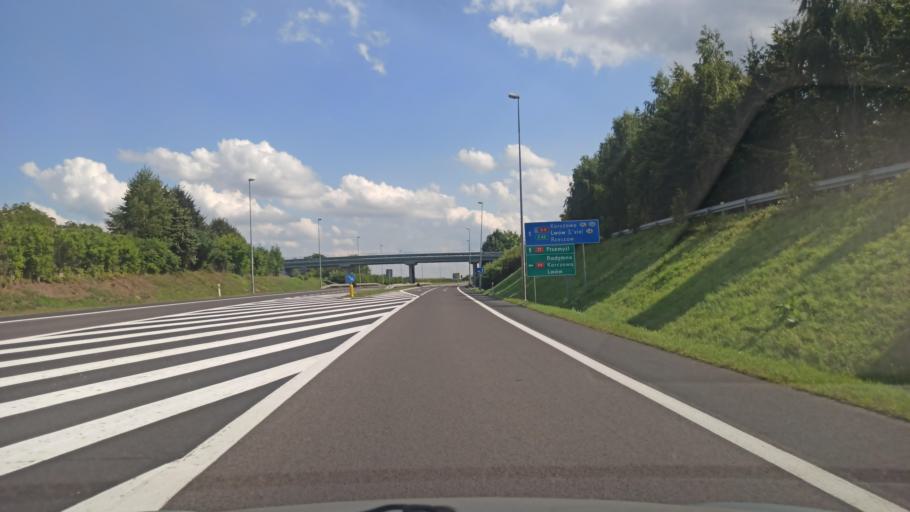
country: PL
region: Subcarpathian Voivodeship
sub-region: Powiat jaroslawski
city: Radymno
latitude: 49.9347
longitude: 22.8179
